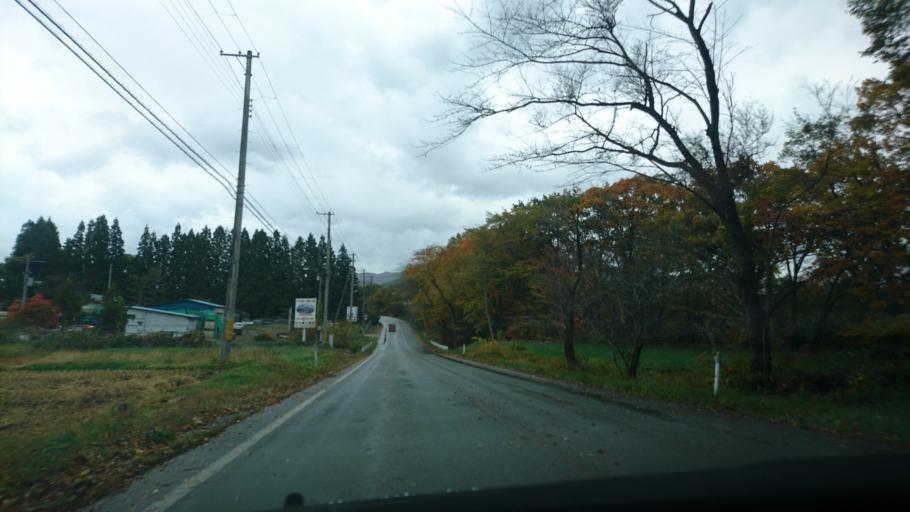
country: JP
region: Iwate
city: Shizukuishi
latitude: 39.6684
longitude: 140.9759
